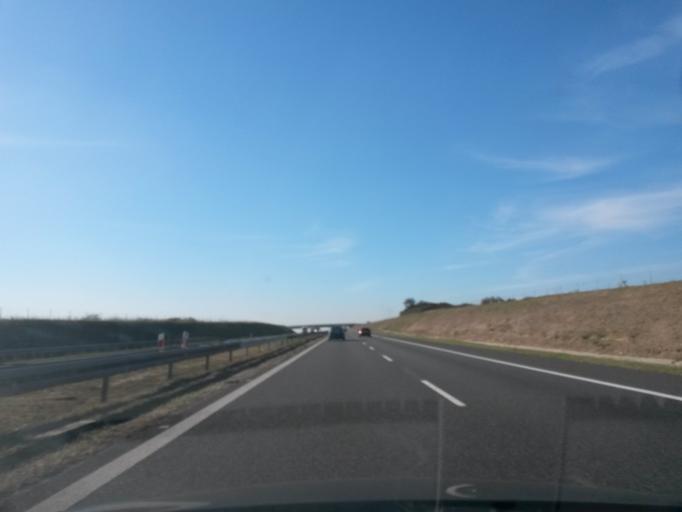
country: PL
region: Opole Voivodeship
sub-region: Powiat krapkowicki
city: Gogolin
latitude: 50.4811
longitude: 18.0575
